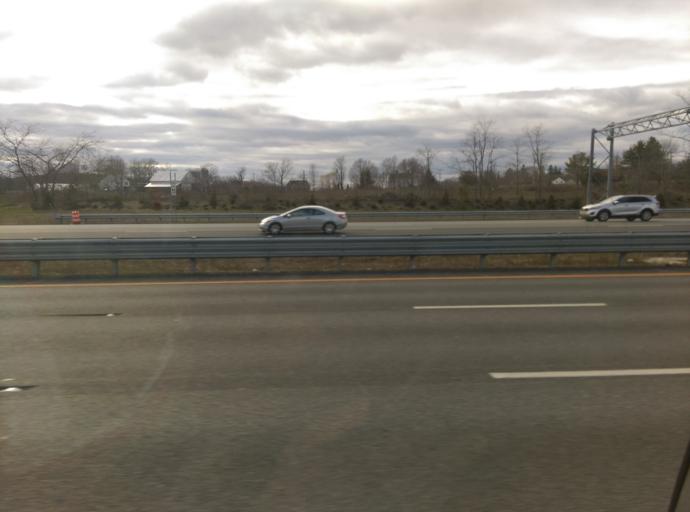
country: US
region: New Hampshire
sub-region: Rockingham County
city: Seabrook
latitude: 42.8653
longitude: -70.8916
